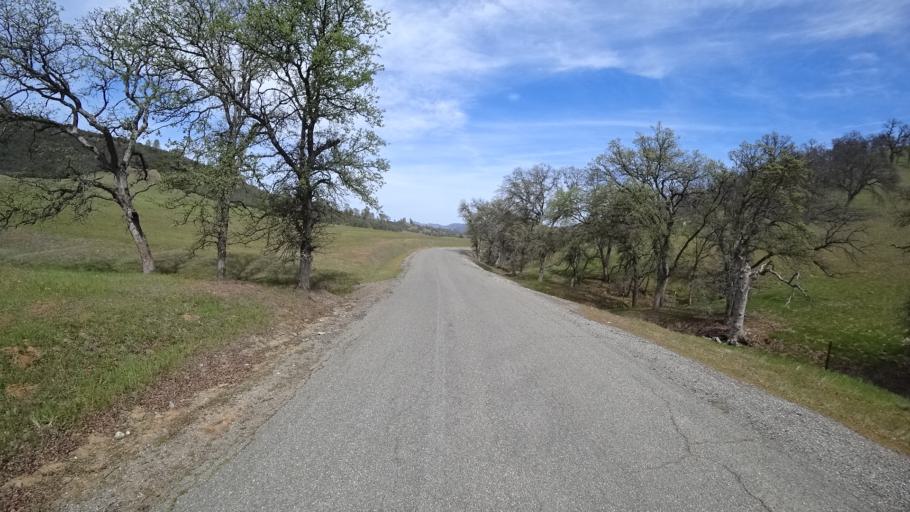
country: US
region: California
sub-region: Glenn County
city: Willows
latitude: 39.6020
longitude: -122.5272
